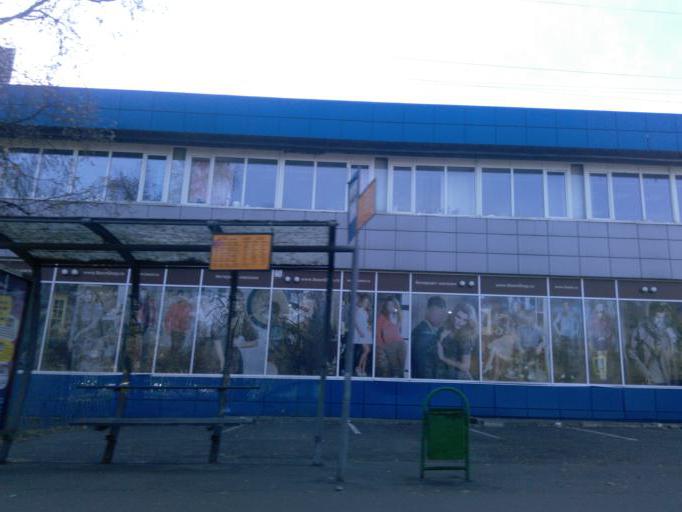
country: RU
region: Moskovskaya
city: Semenovskoye
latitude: 55.6720
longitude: 37.5485
